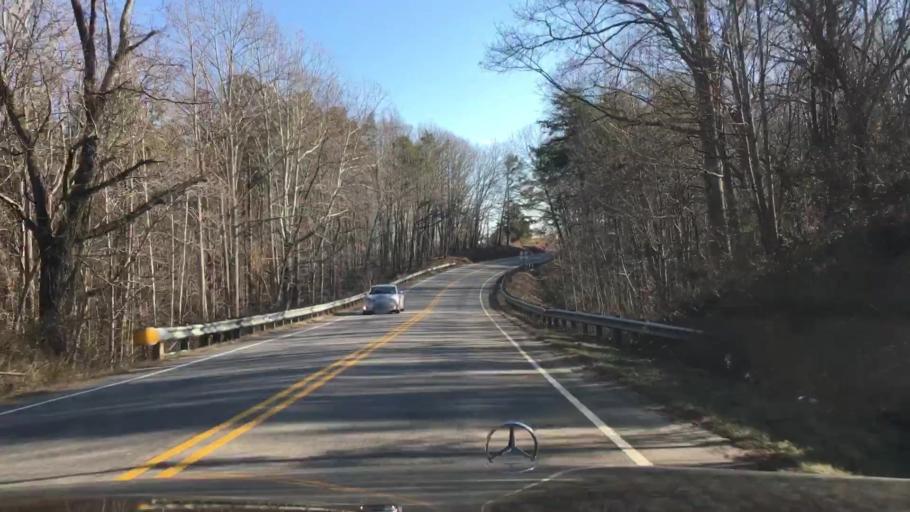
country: US
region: Virginia
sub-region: Campbell County
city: Altavista
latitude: 37.1460
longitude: -79.3139
